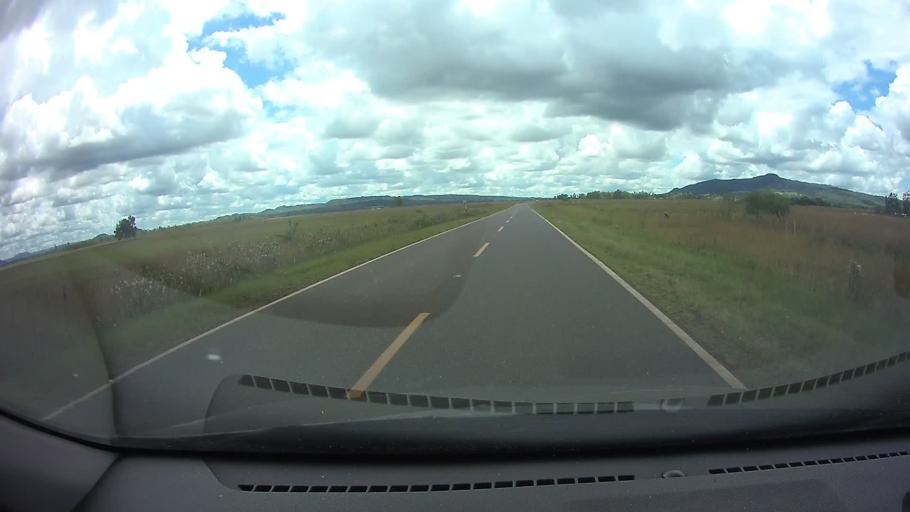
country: PY
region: Paraguari
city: Ybycui
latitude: -25.9109
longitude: -57.0189
